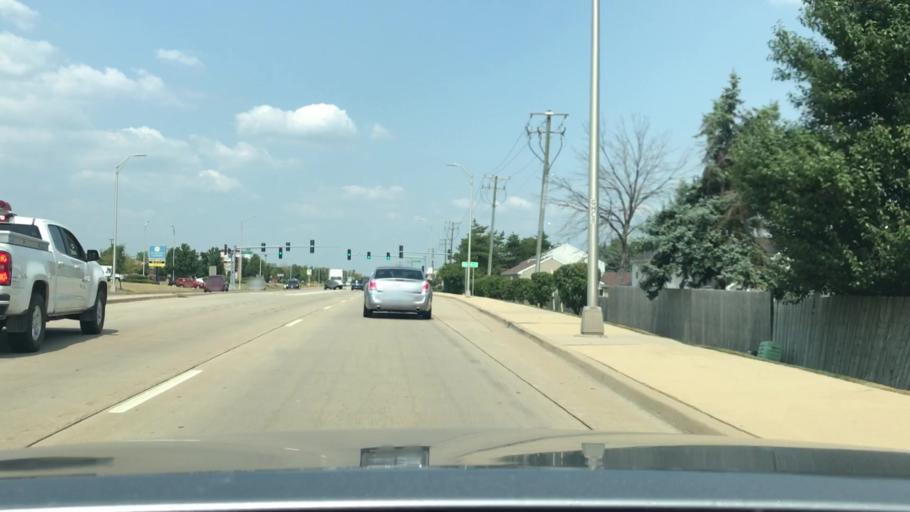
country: US
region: Illinois
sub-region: Will County
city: Shorewood
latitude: 41.5596
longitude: -88.2001
